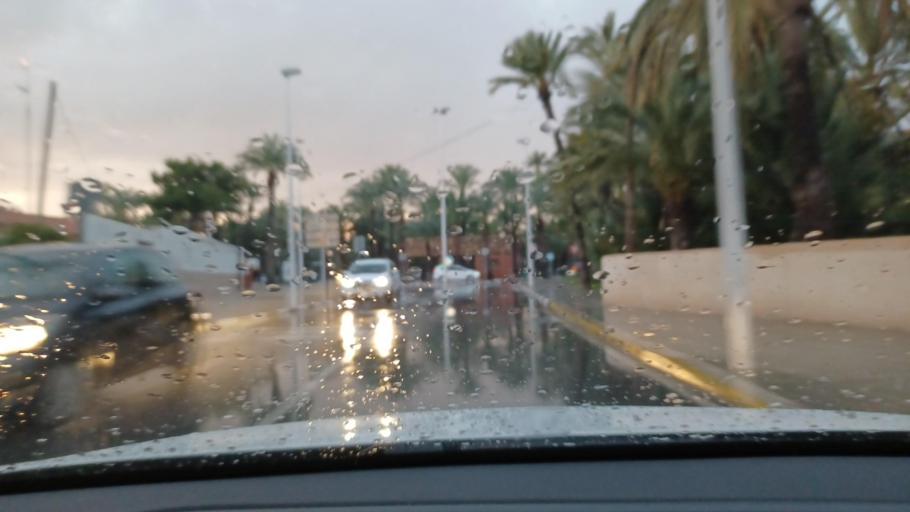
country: ES
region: Valencia
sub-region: Provincia de Alicante
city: Elche
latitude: 38.2582
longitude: -0.6930
